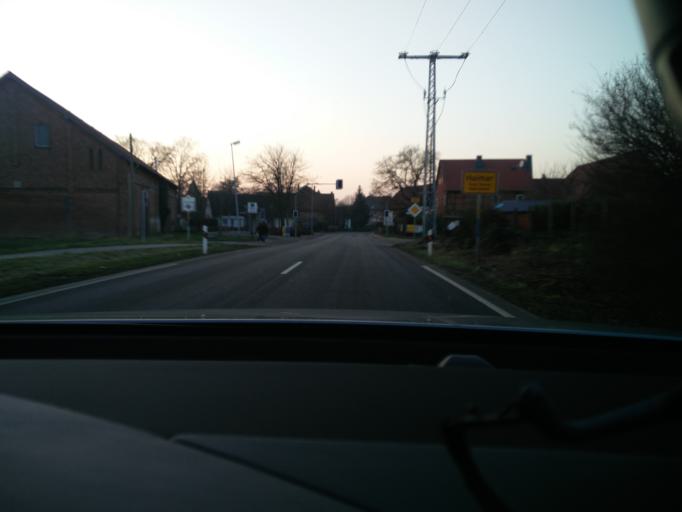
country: DE
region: Lower Saxony
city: Hohenhameln
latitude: 52.3069
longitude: 10.0519
